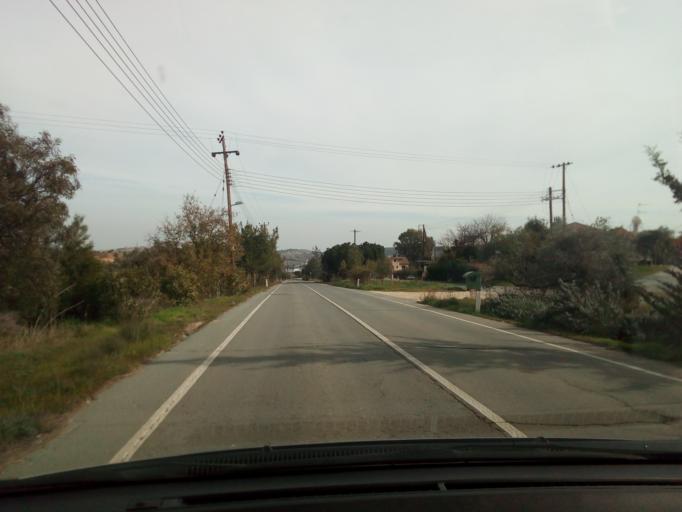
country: CY
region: Lefkosia
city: Klirou
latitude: 35.0412
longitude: 33.1436
